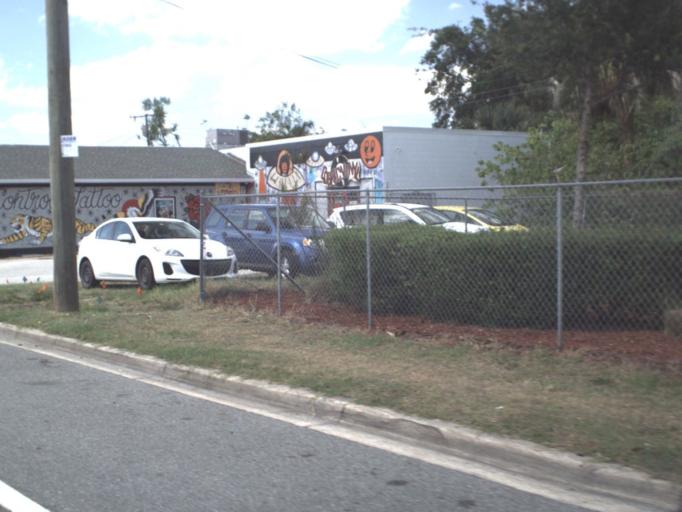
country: US
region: Florida
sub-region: Brevard County
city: Titusville
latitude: 28.5994
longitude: -80.8071
